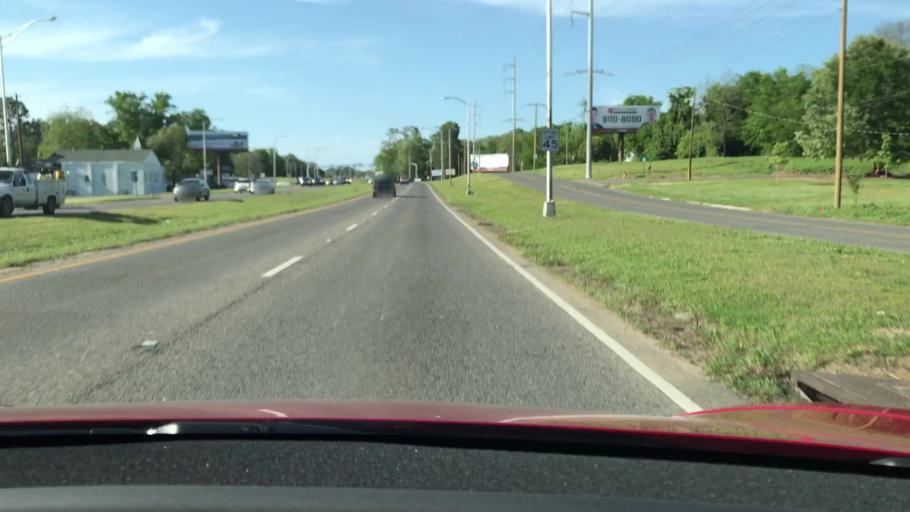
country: US
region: Louisiana
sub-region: Bossier Parish
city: Bossier City
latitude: 32.4901
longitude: -93.7242
